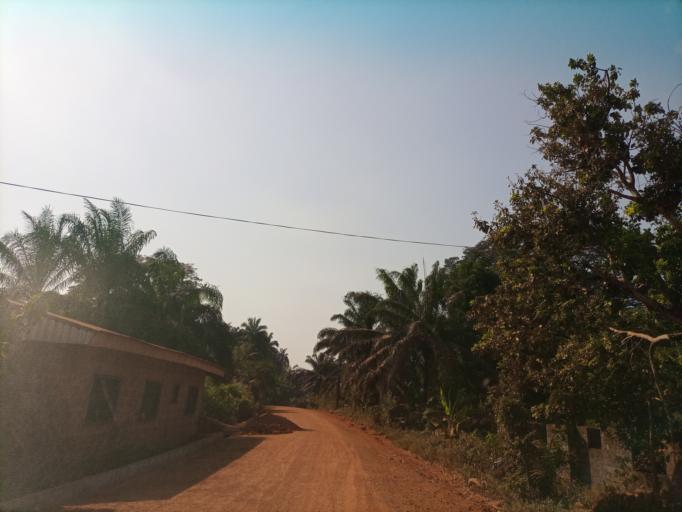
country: NG
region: Enugu
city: Aku
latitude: 6.7005
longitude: 7.3205
